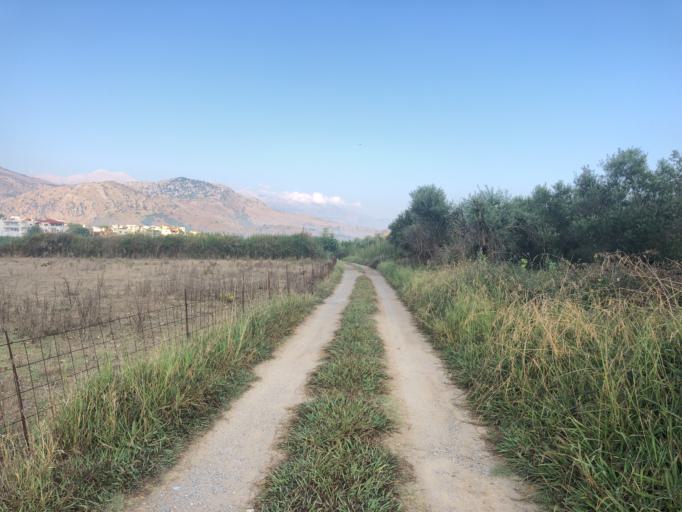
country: GR
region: Crete
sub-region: Nomos Chanias
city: Georgioupolis
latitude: 35.3470
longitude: 24.3059
